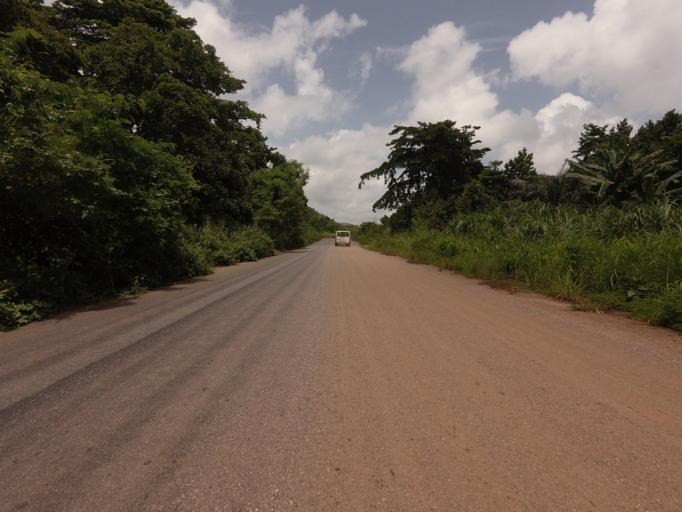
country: GH
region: Volta
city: Kpandu
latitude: 6.8091
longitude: 0.3748
